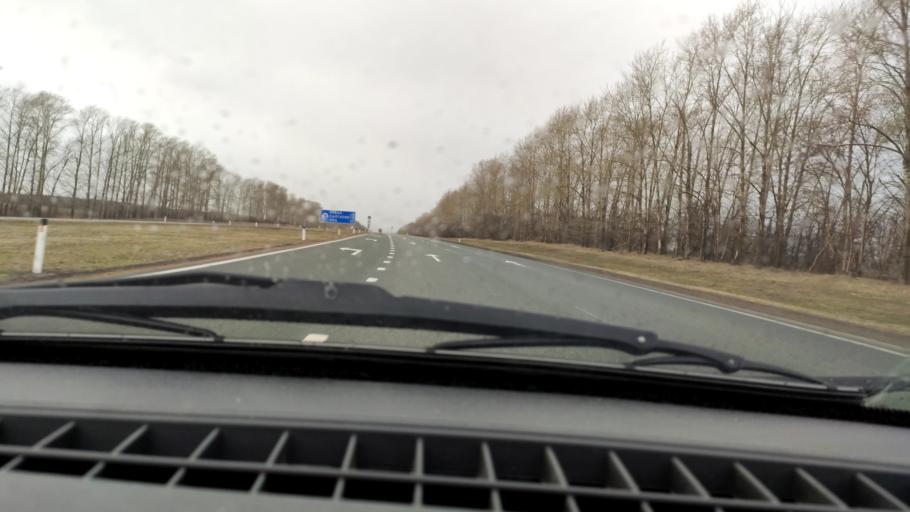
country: RU
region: Bashkortostan
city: Kushnarenkovo
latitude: 55.0293
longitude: 55.4645
